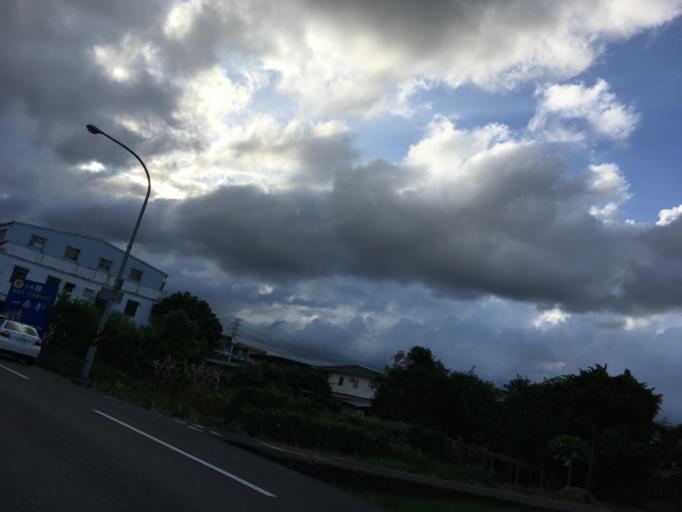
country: TW
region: Taiwan
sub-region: Yilan
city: Yilan
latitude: 24.6550
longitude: 121.7656
